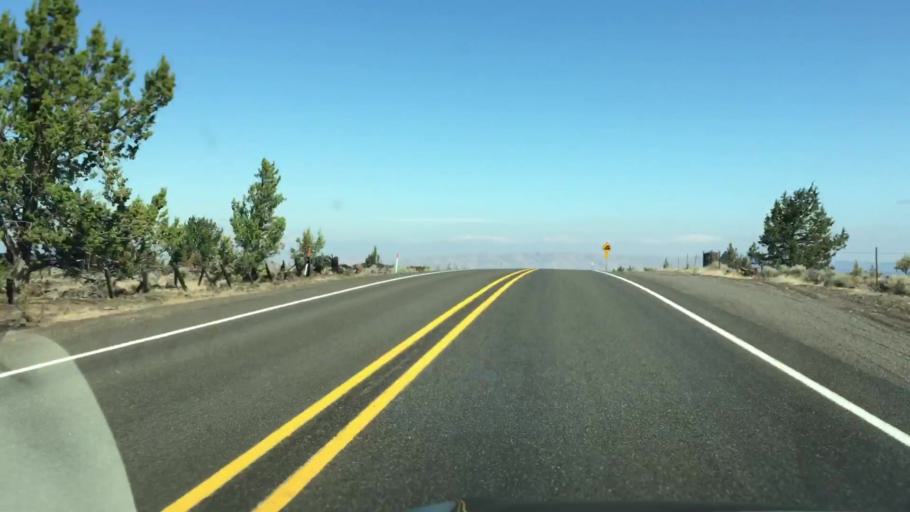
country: US
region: Oregon
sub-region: Jefferson County
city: Warm Springs
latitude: 45.0840
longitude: -121.0261
